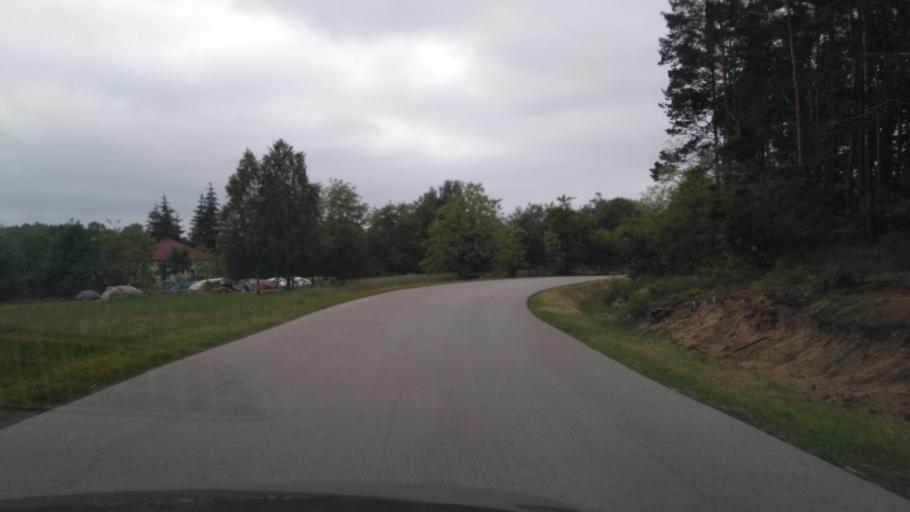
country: PL
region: Subcarpathian Voivodeship
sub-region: Powiat kolbuszowski
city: Niwiska
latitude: 50.2161
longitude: 21.6338
